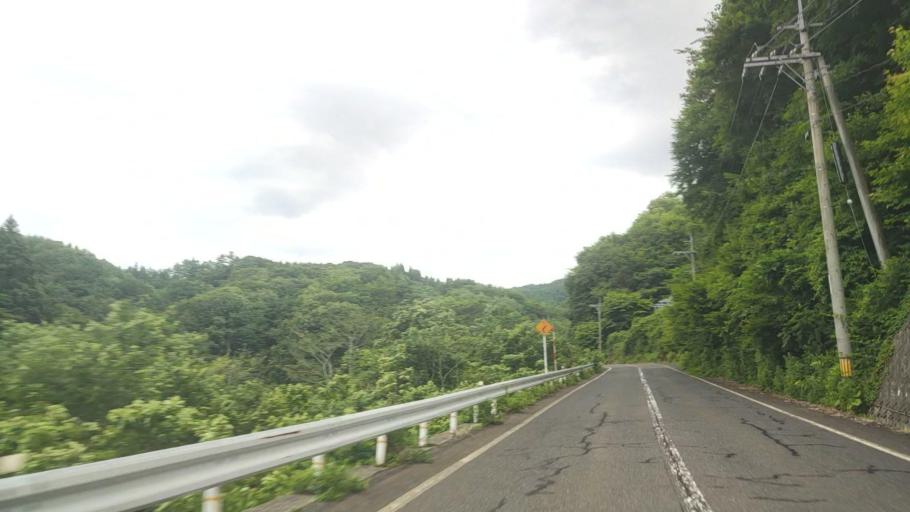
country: JP
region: Tottori
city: Kurayoshi
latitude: 35.3191
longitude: 134.0096
